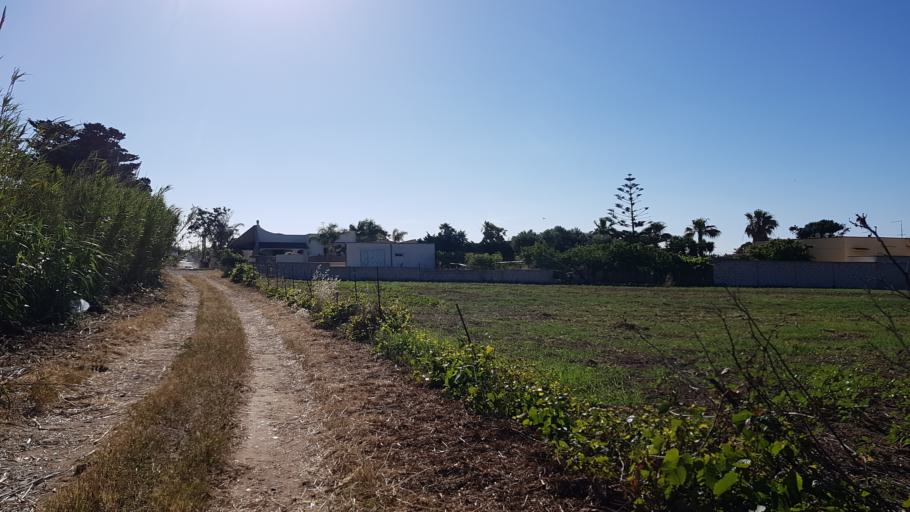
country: IT
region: Apulia
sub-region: Provincia di Brindisi
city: Brindisi
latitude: 40.6813
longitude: 17.8791
